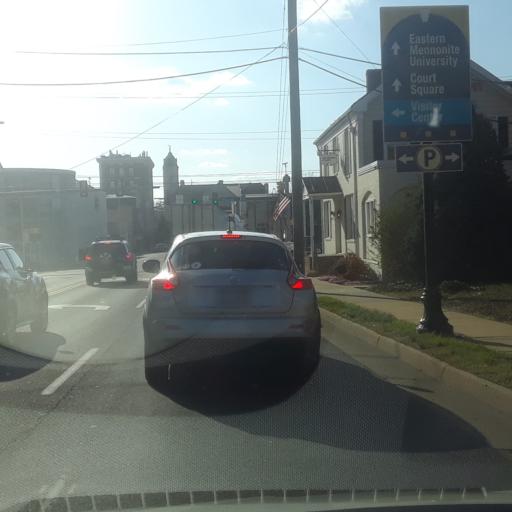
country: US
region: Virginia
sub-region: City of Harrisonburg
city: Harrisonburg
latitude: 38.4490
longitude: -78.8657
